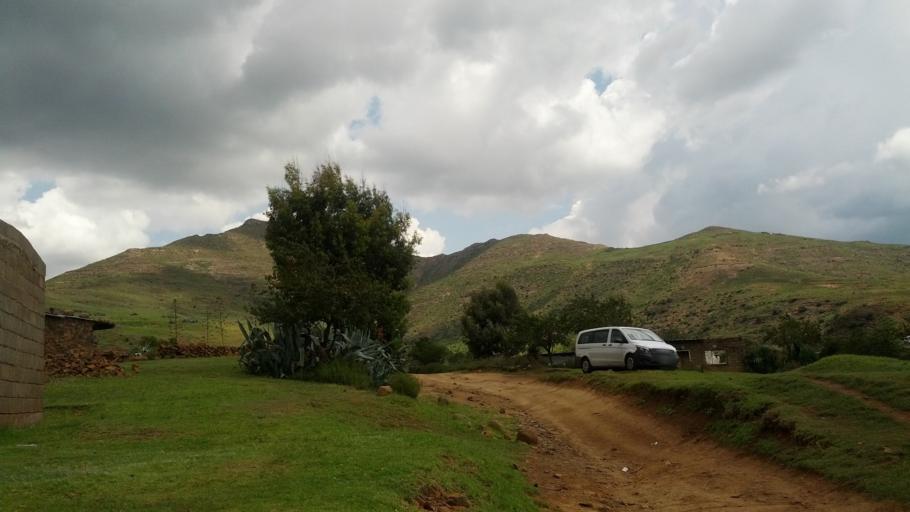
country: LS
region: Maseru
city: Nako
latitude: -29.5911
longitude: 27.7541
